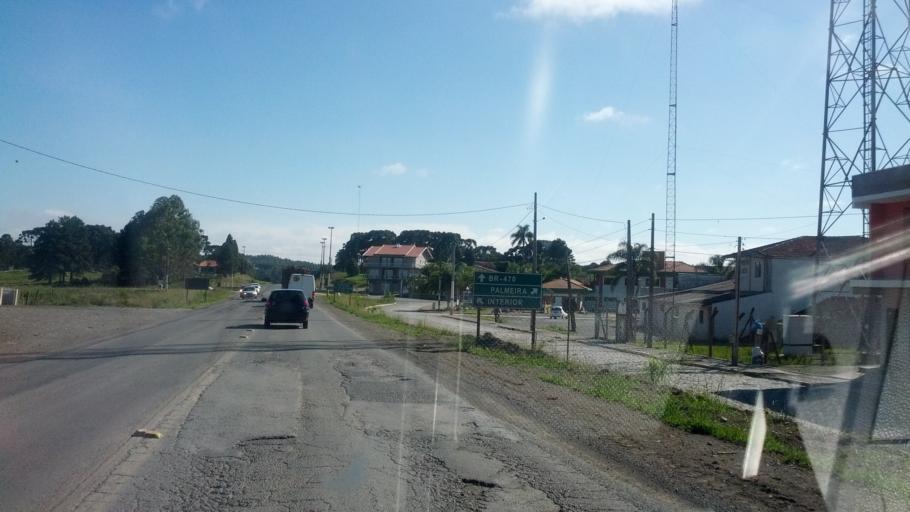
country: BR
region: Santa Catarina
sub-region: Otacilio Costa
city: Otacilio Costa
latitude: -27.5804
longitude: -50.1611
